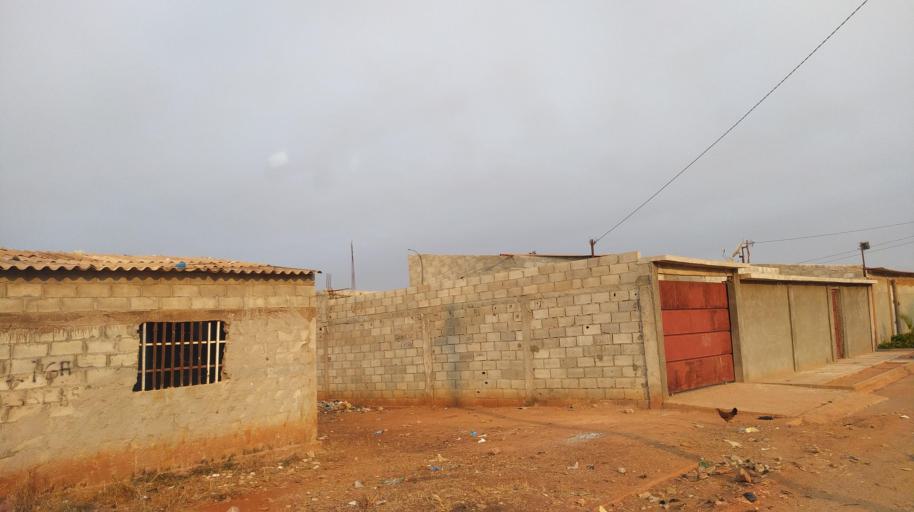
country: AO
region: Luanda
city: Luanda
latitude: -9.0711
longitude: 13.4283
